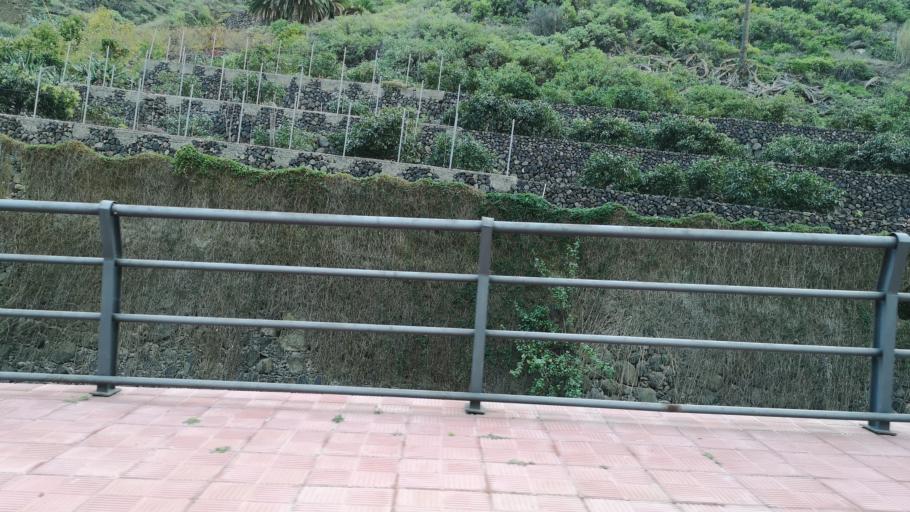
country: ES
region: Canary Islands
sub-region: Provincia de Santa Cruz de Tenerife
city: Hermigua
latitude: 28.1671
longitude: -17.1946
